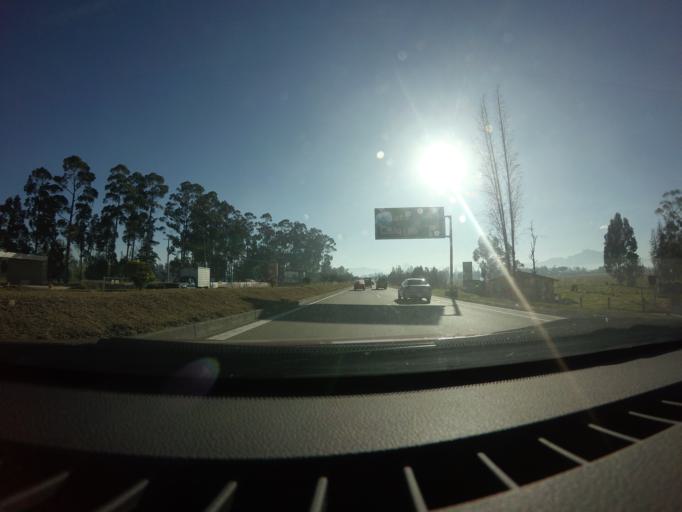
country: CO
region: Cundinamarca
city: Zipaquira
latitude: 4.9946
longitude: -73.9966
